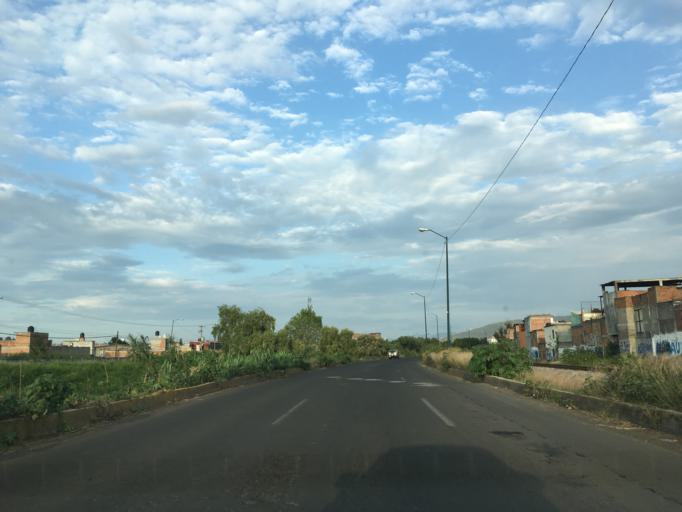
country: MX
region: Michoacan
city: Morelia
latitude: 19.7144
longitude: -101.2051
